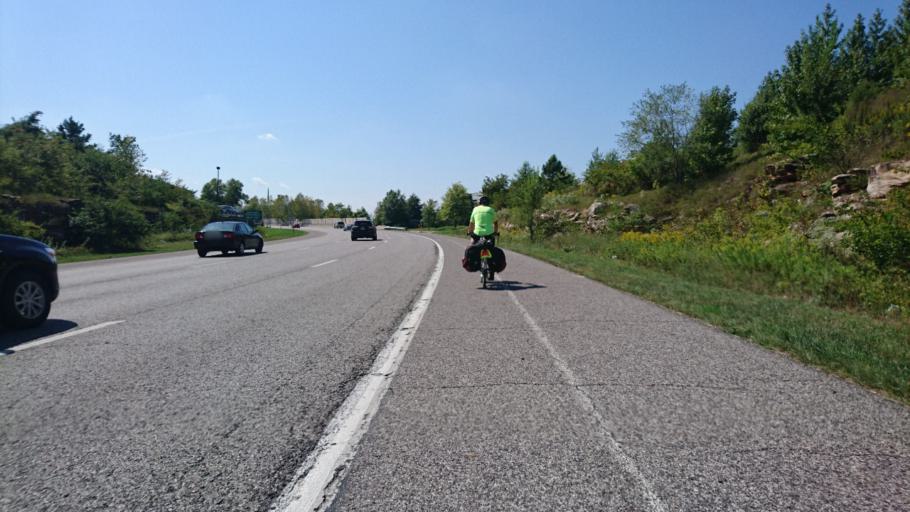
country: US
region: Missouri
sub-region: Saint Louis County
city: Town and Country
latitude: 38.6036
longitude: -90.4653
